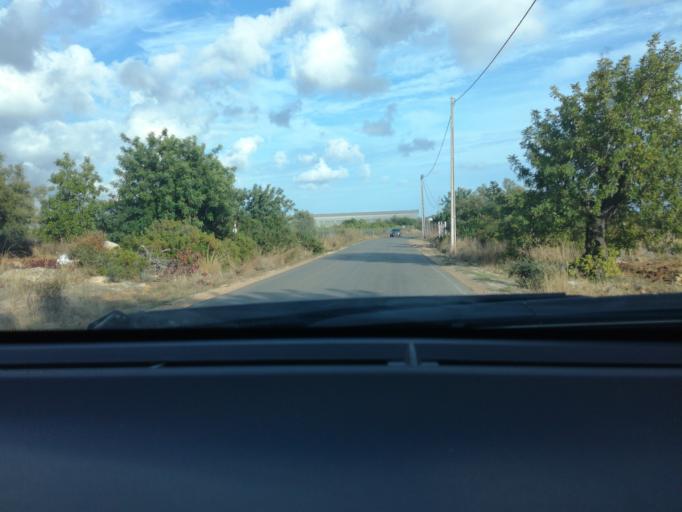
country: PT
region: Faro
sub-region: Olhao
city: Olhao
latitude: 37.0821
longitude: -7.8462
